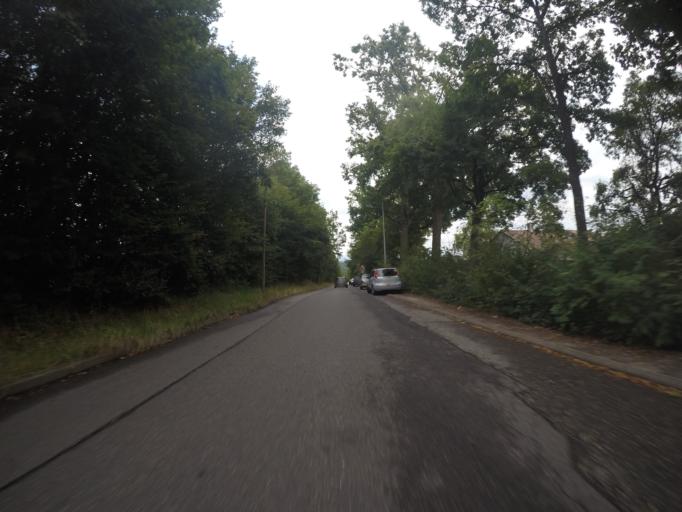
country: DE
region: Baden-Wuerttemberg
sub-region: Regierungsbezirk Stuttgart
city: Ostfildern
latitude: 48.7340
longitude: 9.2003
